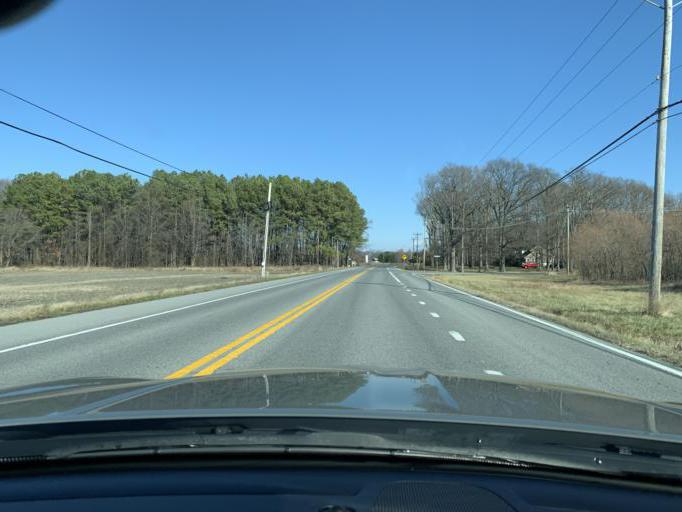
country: US
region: Maryland
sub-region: Queen Anne's County
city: Centreville
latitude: 39.0725
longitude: -76.0472
